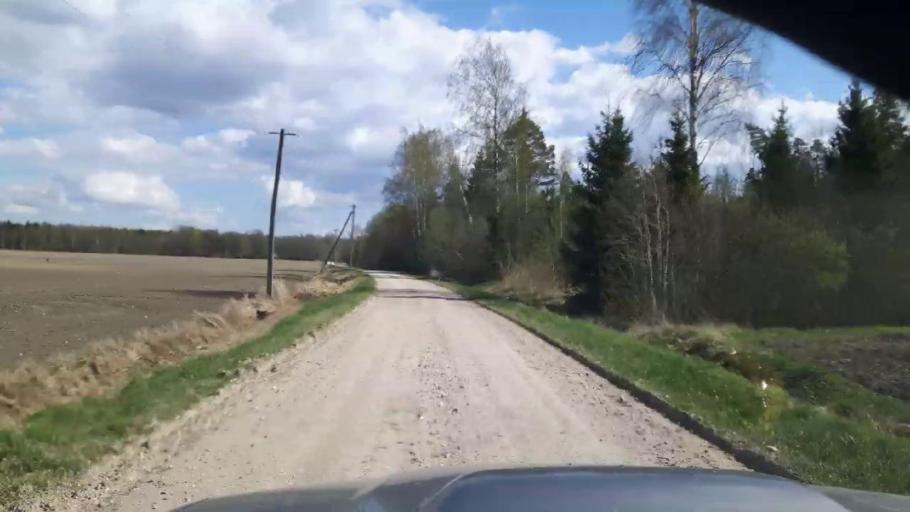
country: EE
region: Paernumaa
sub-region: Tootsi vald
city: Tootsi
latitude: 58.4578
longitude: 24.8093
